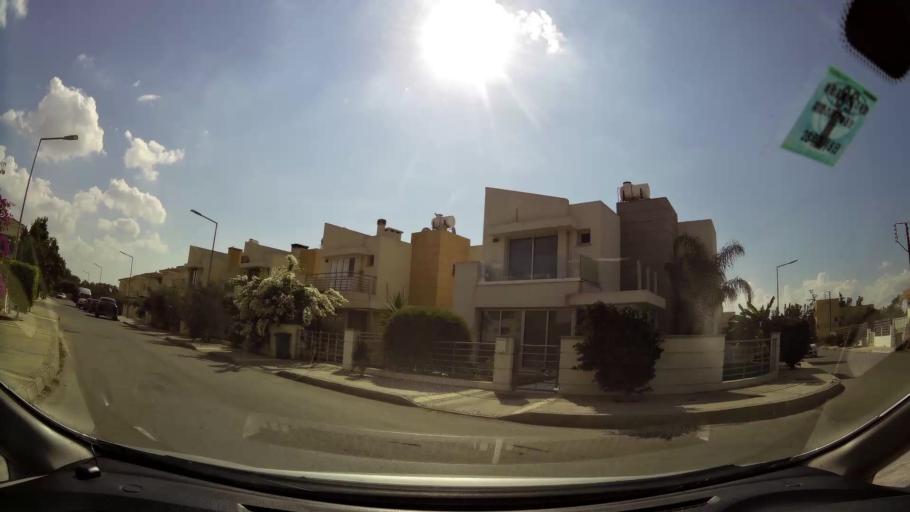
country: CY
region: Lefkosia
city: Nicosia
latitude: 35.2169
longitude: 33.3815
